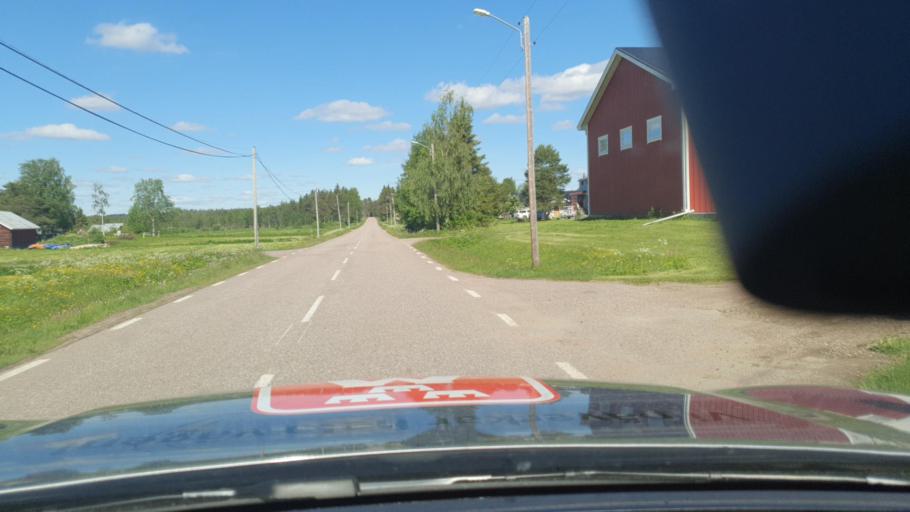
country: SE
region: Norrbotten
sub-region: Overkalix Kommun
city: OEverkalix
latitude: 67.0039
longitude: 22.4930
